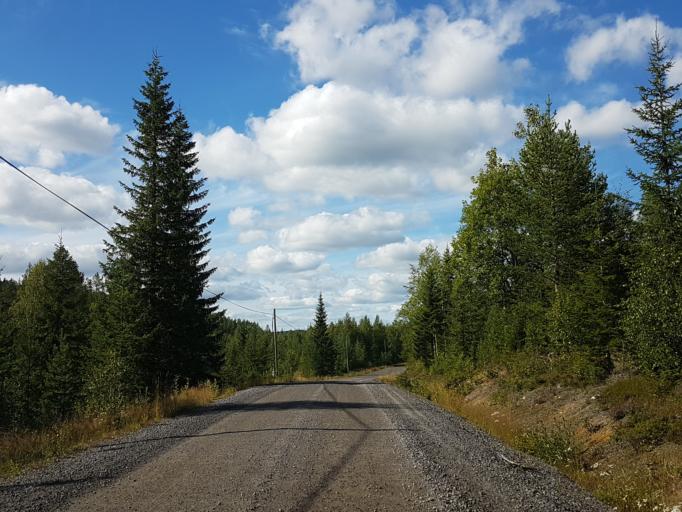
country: SE
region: Vaesterbotten
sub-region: Skelleftea Kommun
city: Burtraesk
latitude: 64.2847
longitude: 20.4618
